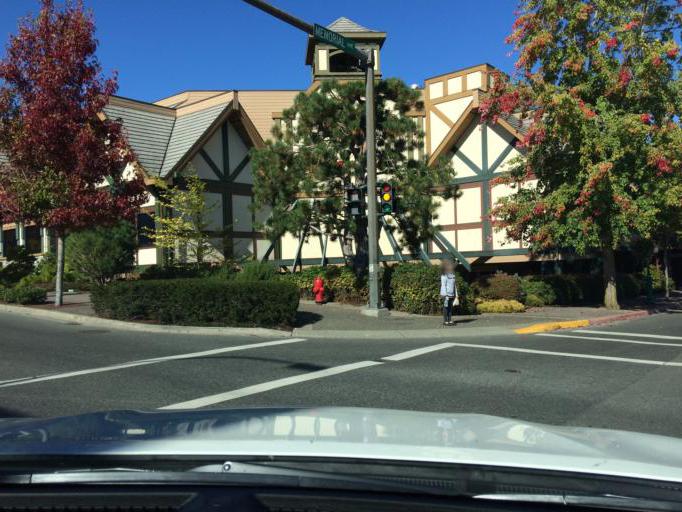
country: CA
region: British Columbia
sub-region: Regional District of Nanaimo
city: Parksville
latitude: 49.3459
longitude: -124.4417
